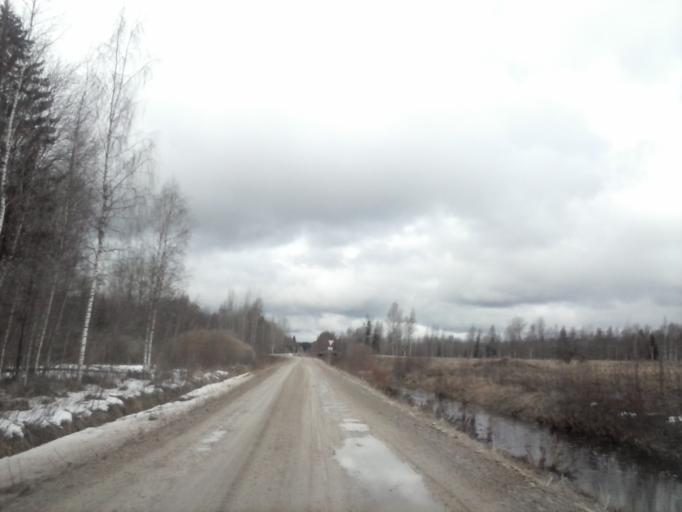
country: EE
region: Jogevamaa
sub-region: Mustvee linn
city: Mustvee
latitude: 59.0818
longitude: 26.8723
